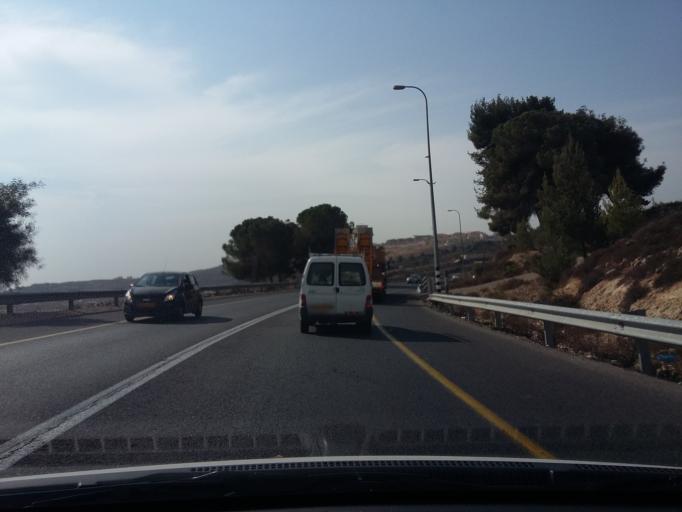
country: PS
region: West Bank
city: Al Khadir
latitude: 31.6910
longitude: 35.1624
